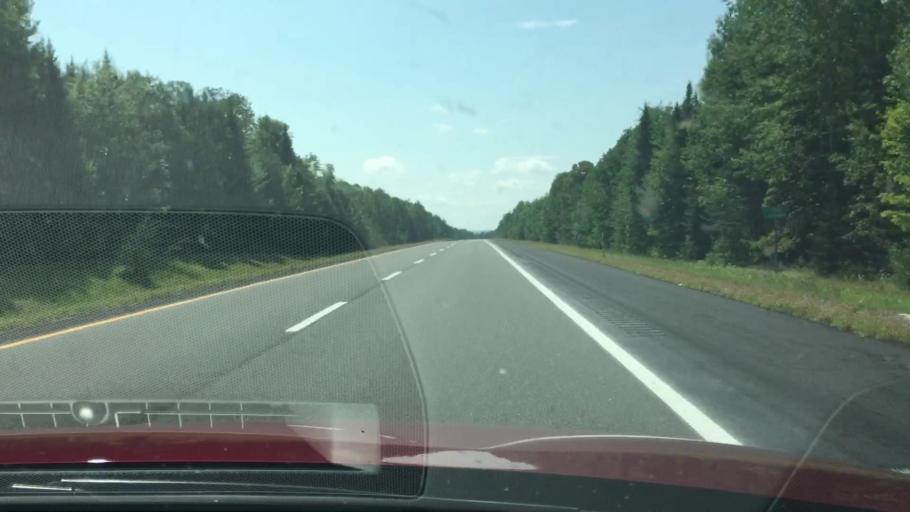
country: US
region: Maine
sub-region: Penobscot County
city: Patten
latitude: 45.9450
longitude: -68.3421
